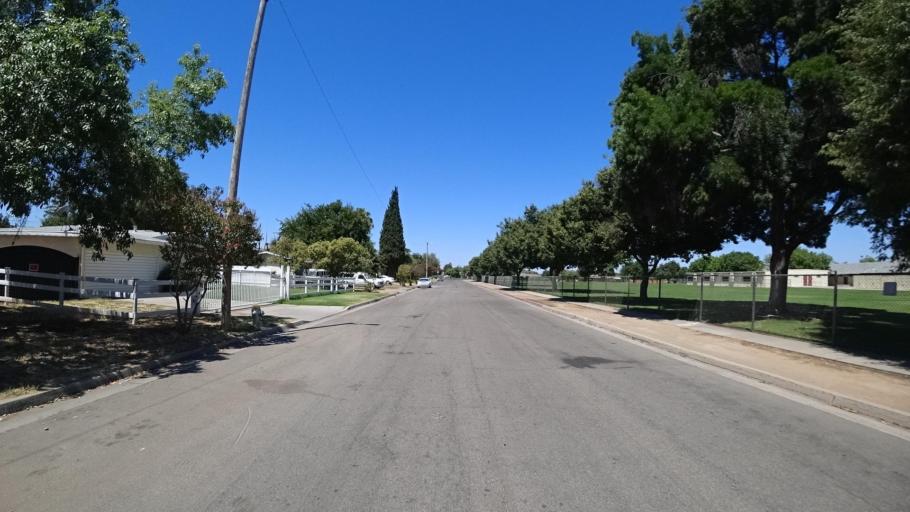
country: US
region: California
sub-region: Fresno County
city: Fresno
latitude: 36.7668
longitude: -119.7432
